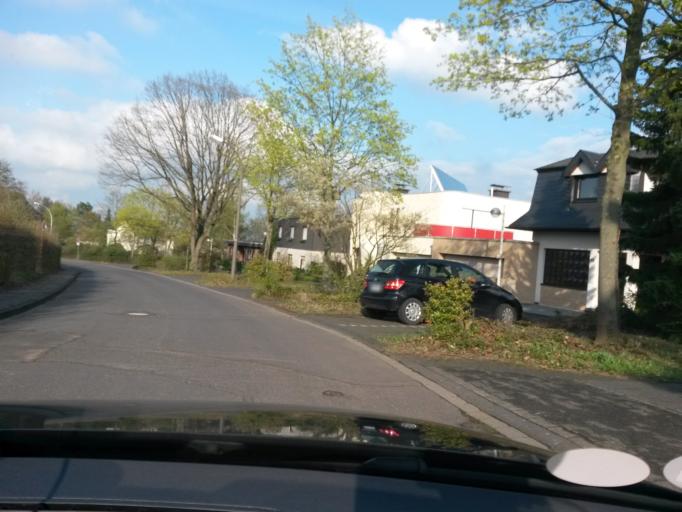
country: DE
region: North Rhine-Westphalia
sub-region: Regierungsbezirk Koln
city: Alfter
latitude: 50.7067
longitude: 7.0366
